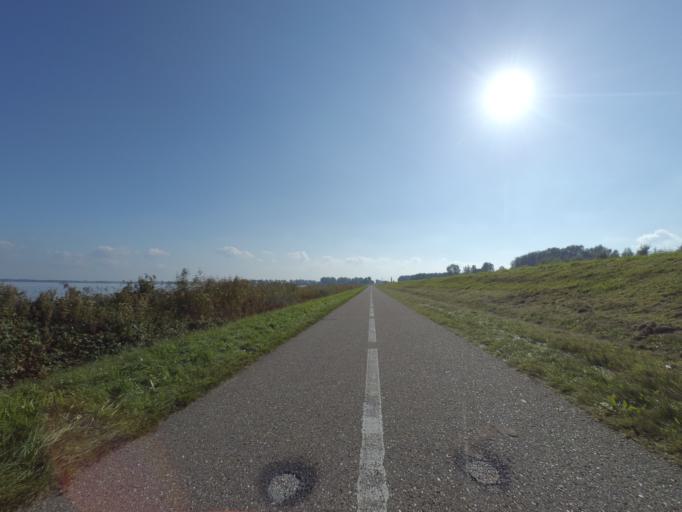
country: NL
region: Flevoland
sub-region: Gemeente Zeewolde
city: Zeewolde
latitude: 52.3413
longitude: 5.5397
